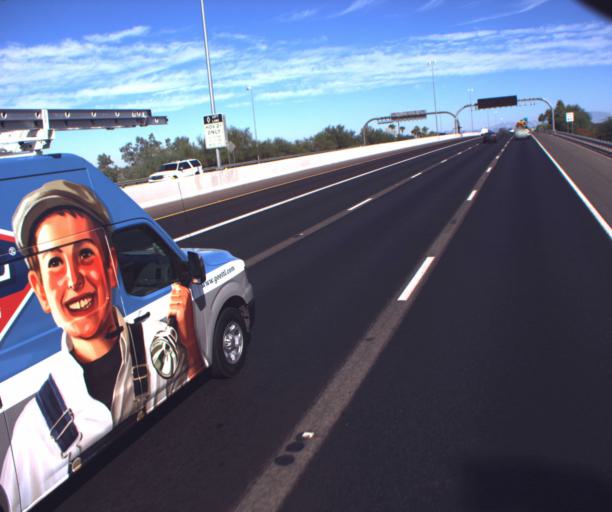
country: US
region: Arizona
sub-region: Maricopa County
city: Peoria
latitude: 33.5783
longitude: -112.2587
